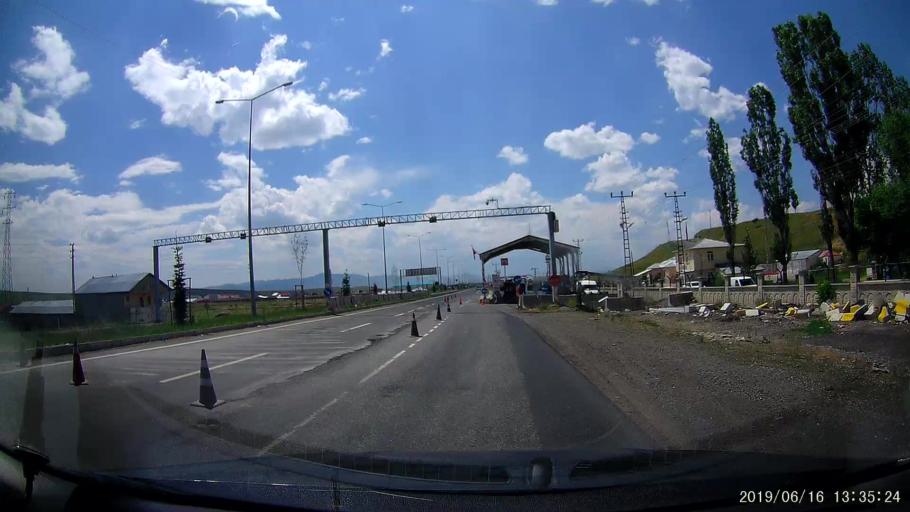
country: TR
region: Agri
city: Agri
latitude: 39.7129
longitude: 43.1108
